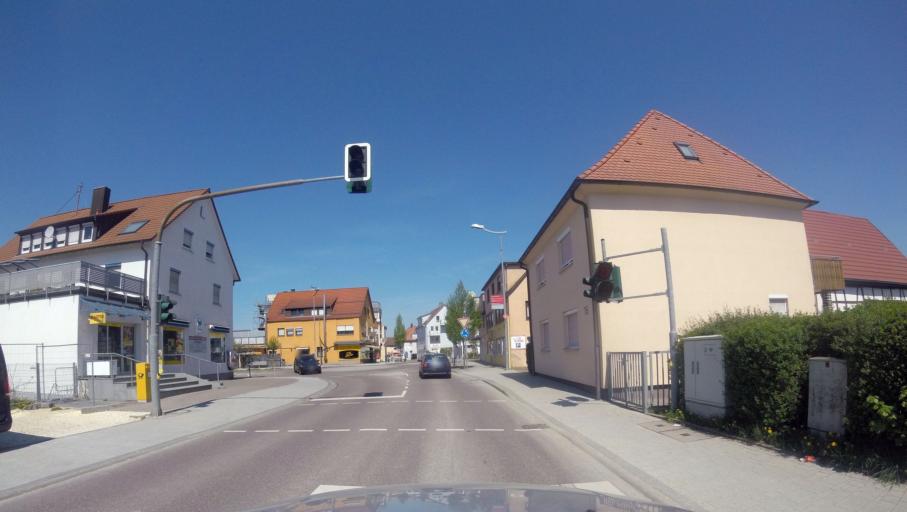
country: DE
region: Baden-Wuerttemberg
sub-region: Regierungsbezirk Stuttgart
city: Mutlangen
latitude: 48.8230
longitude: 9.7979
